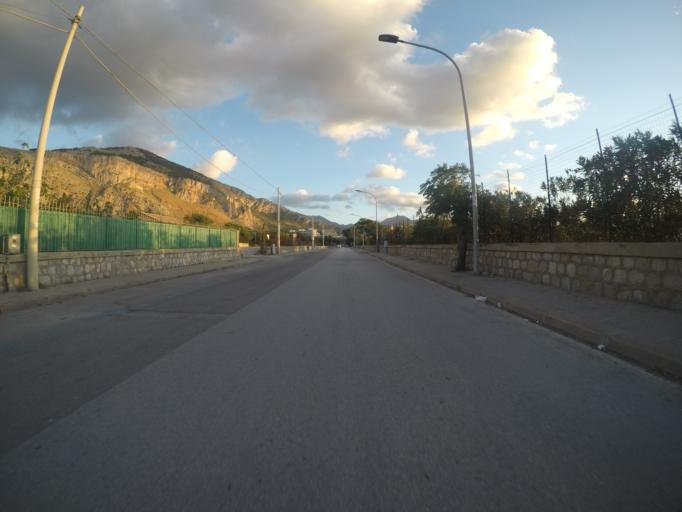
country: IT
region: Sicily
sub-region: Palermo
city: Isola delle Femmine
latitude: 38.1842
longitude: 13.2380
